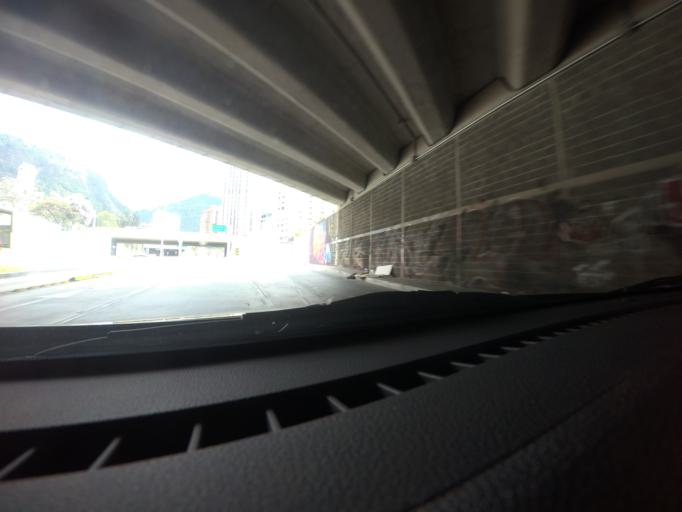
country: CO
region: Bogota D.C.
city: Bogota
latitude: 4.6120
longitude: -74.0708
